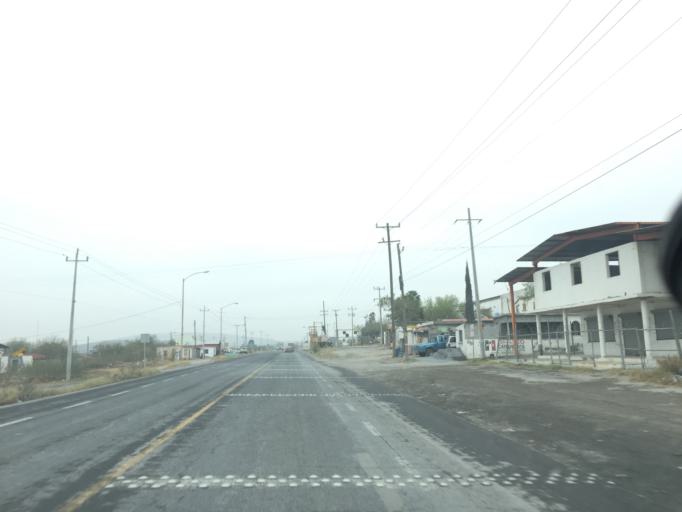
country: MX
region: Nuevo Leon
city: Mina
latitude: 26.0029
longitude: -100.5307
